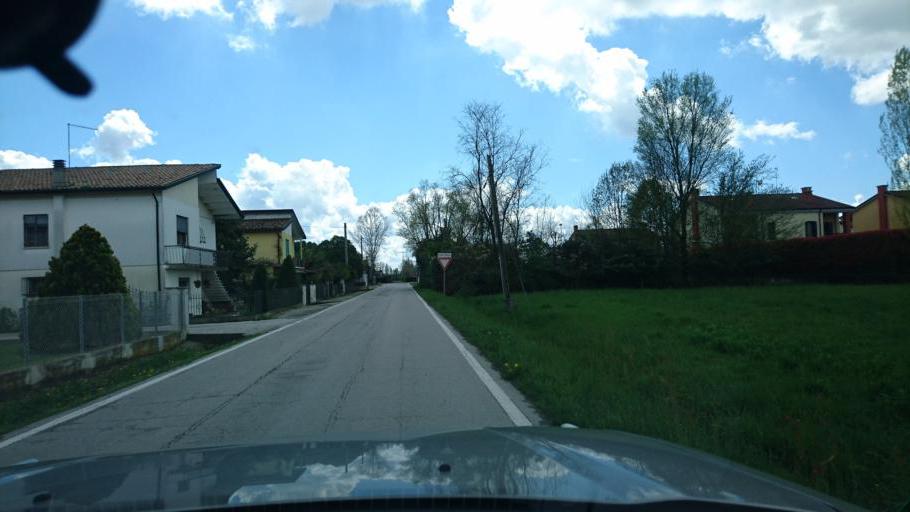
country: IT
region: Veneto
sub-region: Provincia di Padova
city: Piazzola sul Brenta
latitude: 45.5411
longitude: 11.7684
